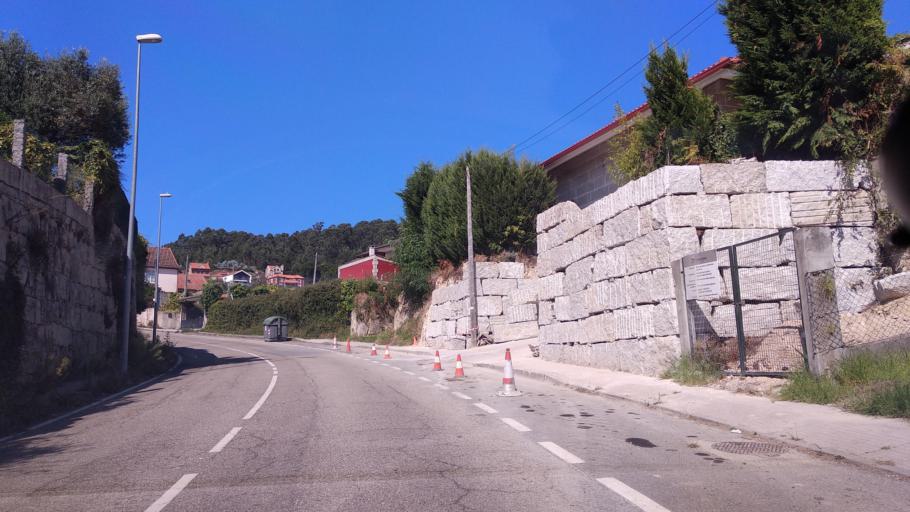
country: ES
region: Galicia
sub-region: Provincia de Pontevedra
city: Moana
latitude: 42.2771
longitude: -8.7685
